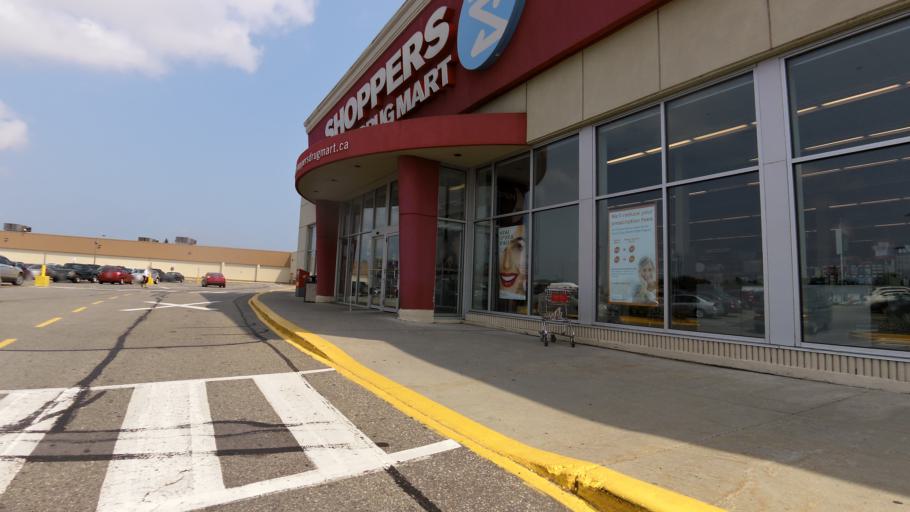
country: CA
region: Ontario
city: Brockville
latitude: 44.6026
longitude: -75.6997
